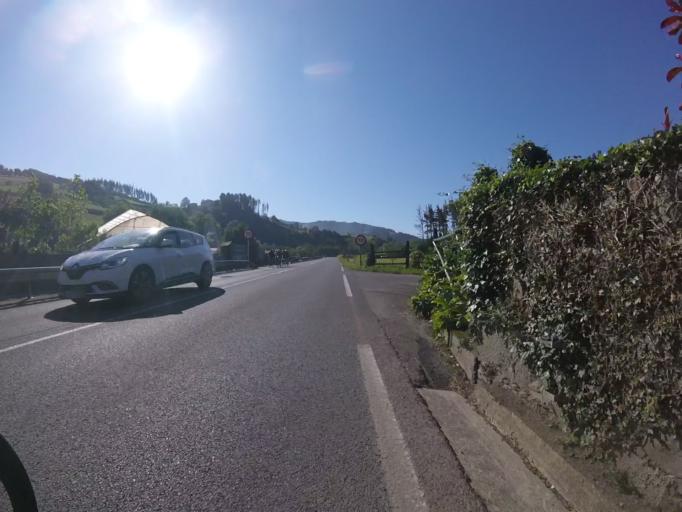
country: ES
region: Basque Country
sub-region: Provincia de Guipuzcoa
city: Azpeitia
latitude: 43.1697
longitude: -2.2524
